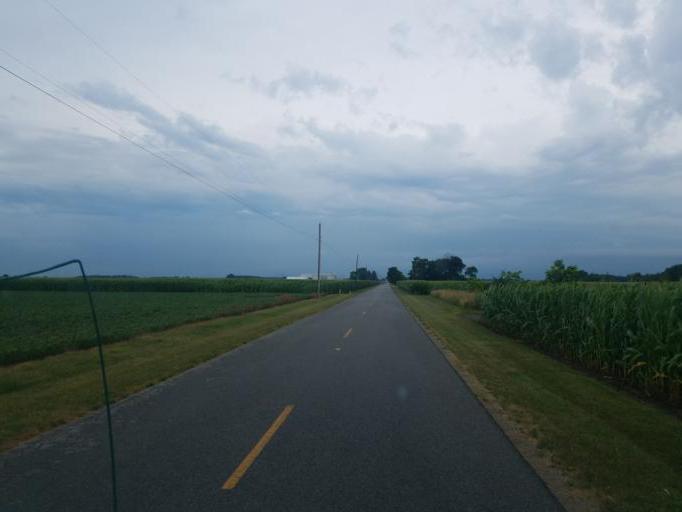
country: US
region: Ohio
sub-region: Paulding County
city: Antwerp
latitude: 41.2373
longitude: -84.7363
